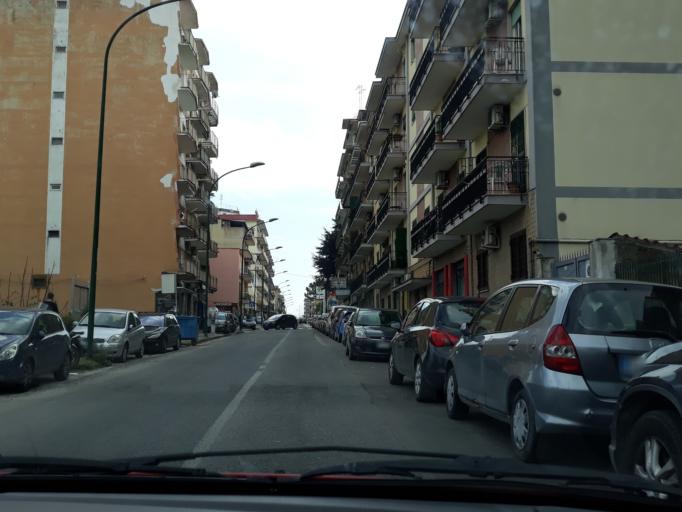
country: IT
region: Campania
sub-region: Provincia di Napoli
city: Napoli
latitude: 40.8835
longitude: 14.2305
